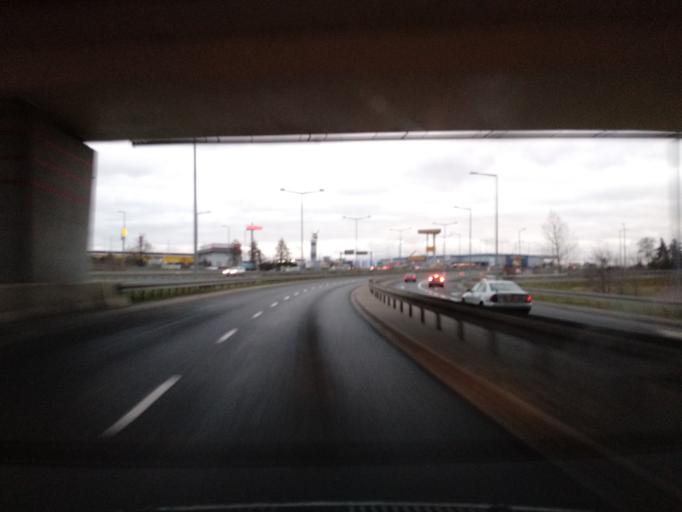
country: PL
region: Greater Poland Voivodeship
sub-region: Powiat koninski
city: Stare Miasto
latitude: 52.1882
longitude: 18.2283
